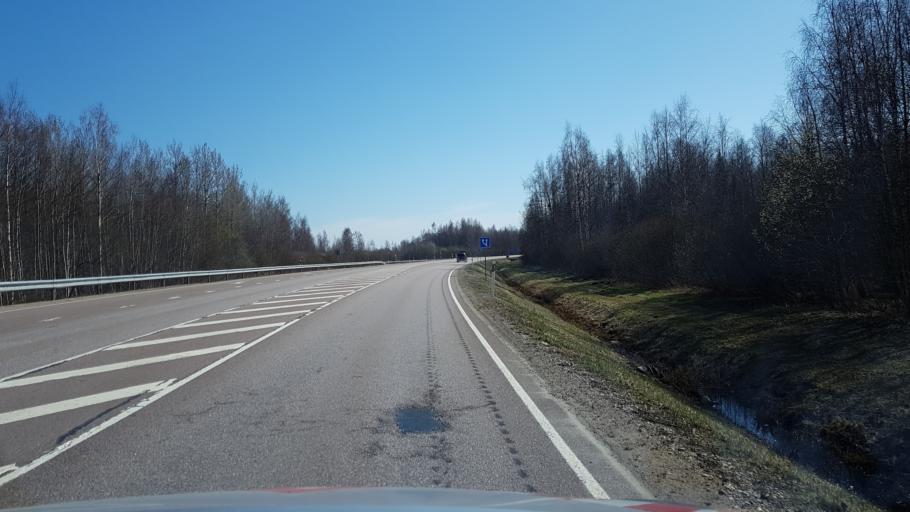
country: EE
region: Jogevamaa
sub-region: Mustvee linn
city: Mustvee
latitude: 58.8282
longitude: 26.9385
